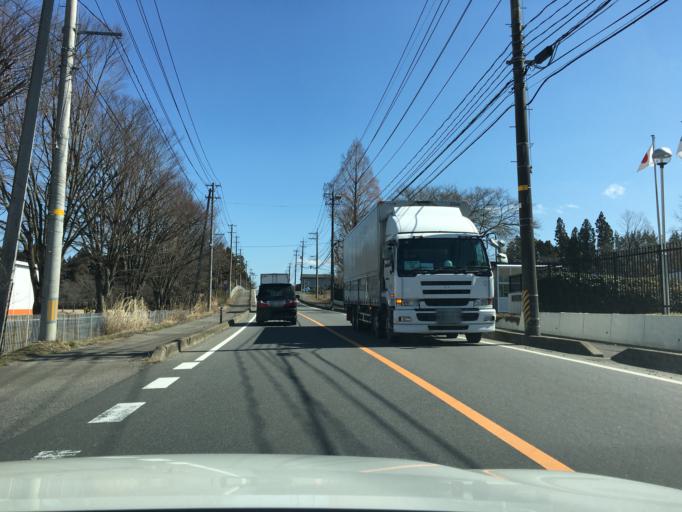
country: JP
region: Tochigi
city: Kuroiso
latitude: 37.1003
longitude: 140.1778
